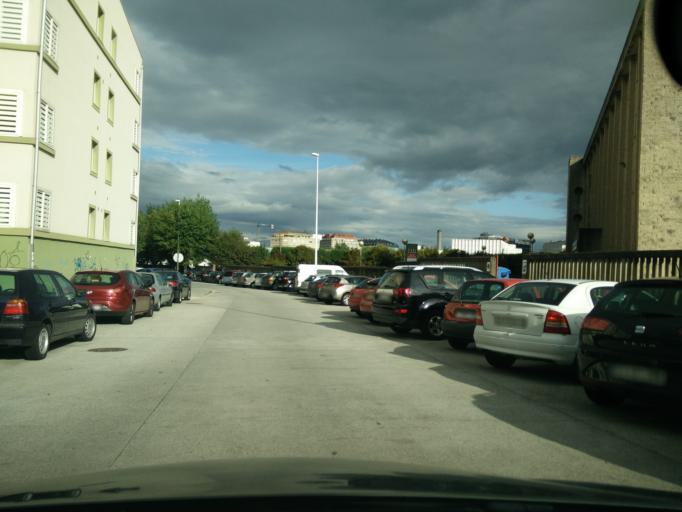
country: ES
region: Galicia
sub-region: Provincia da Coruna
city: A Coruna
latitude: 43.3707
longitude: -8.4246
